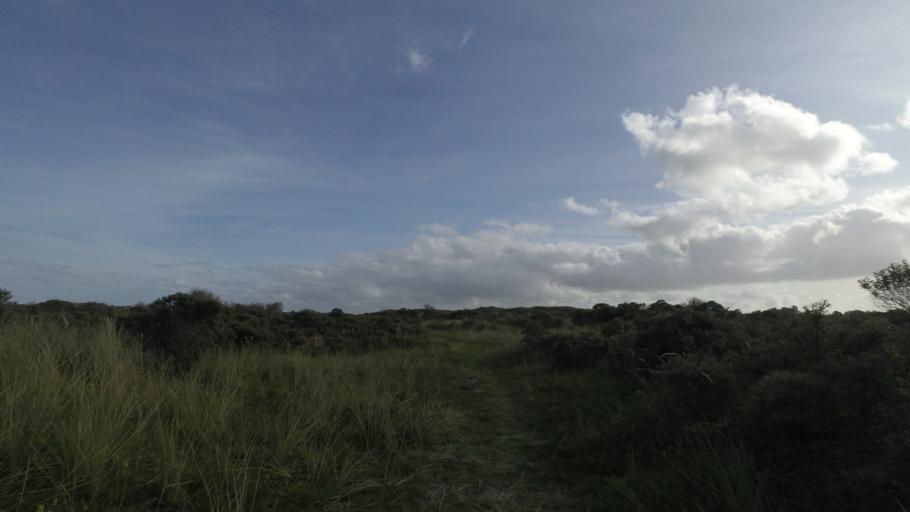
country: NL
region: Friesland
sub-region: Gemeente Ameland
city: Nes
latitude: 53.4577
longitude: 5.8358
